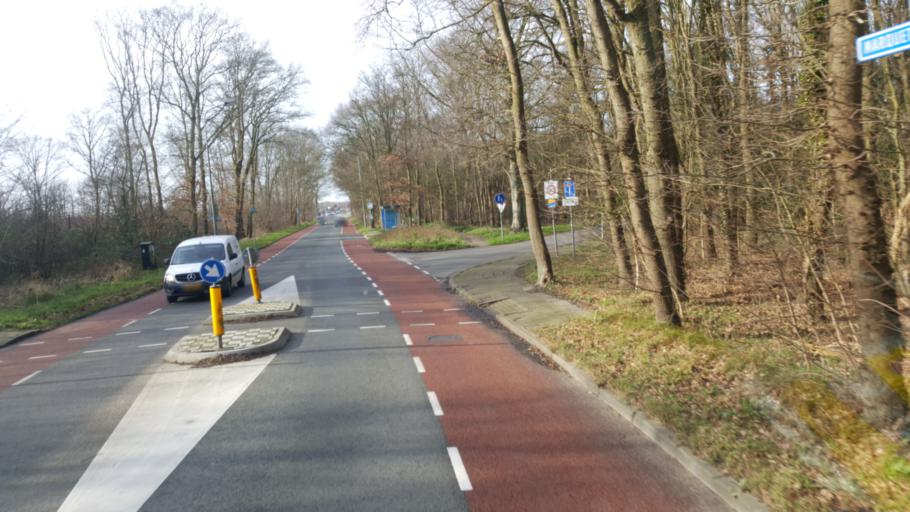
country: NL
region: North Holland
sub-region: Gemeente Heemskerk
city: Heemskerk
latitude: 52.5163
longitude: 4.6582
